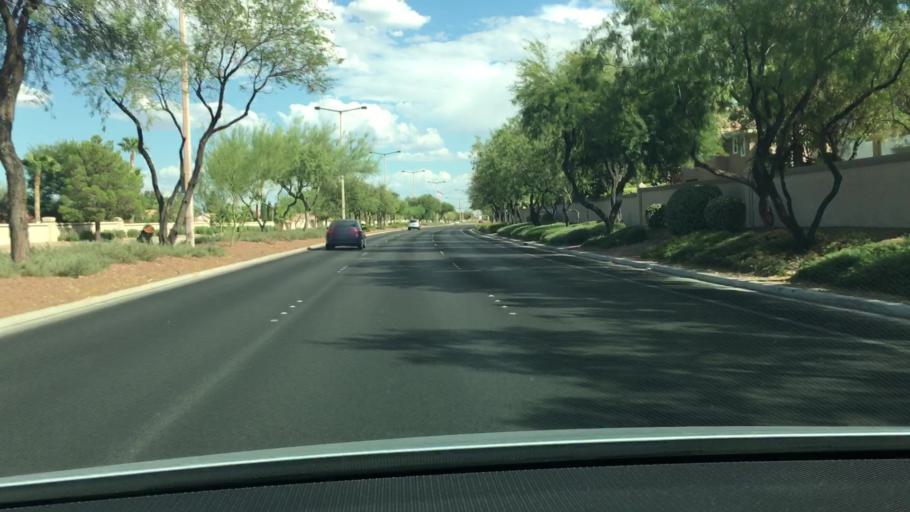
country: US
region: Nevada
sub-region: Clark County
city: Summerlin South
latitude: 36.2036
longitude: -115.2887
